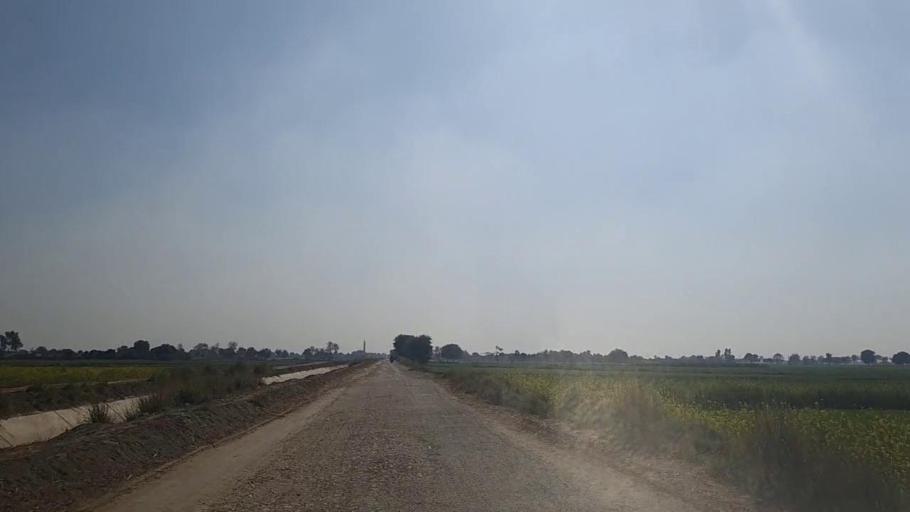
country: PK
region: Sindh
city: Shahpur Chakar
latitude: 26.1978
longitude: 68.5836
